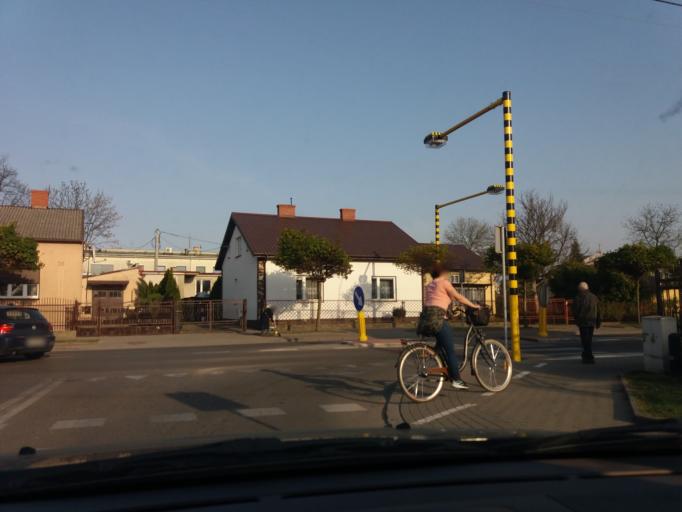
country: PL
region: Masovian Voivodeship
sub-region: Powiat mlawski
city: Mlawa
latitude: 53.1231
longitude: 20.3776
